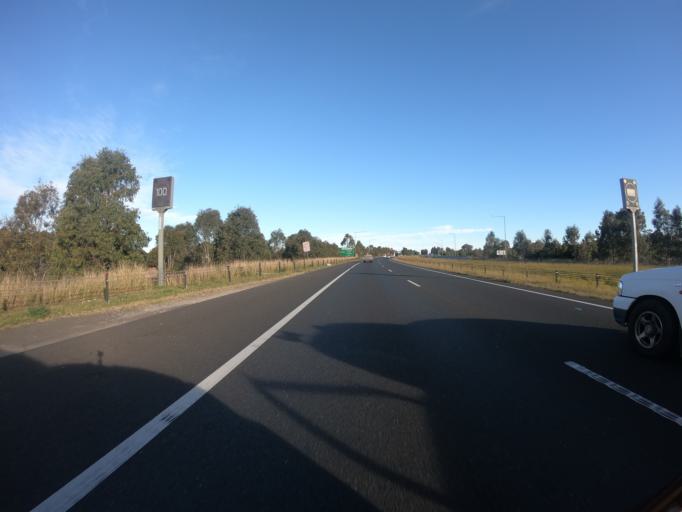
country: AU
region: New South Wales
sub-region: Blacktown
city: Doonside
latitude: -33.7821
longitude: 150.8585
